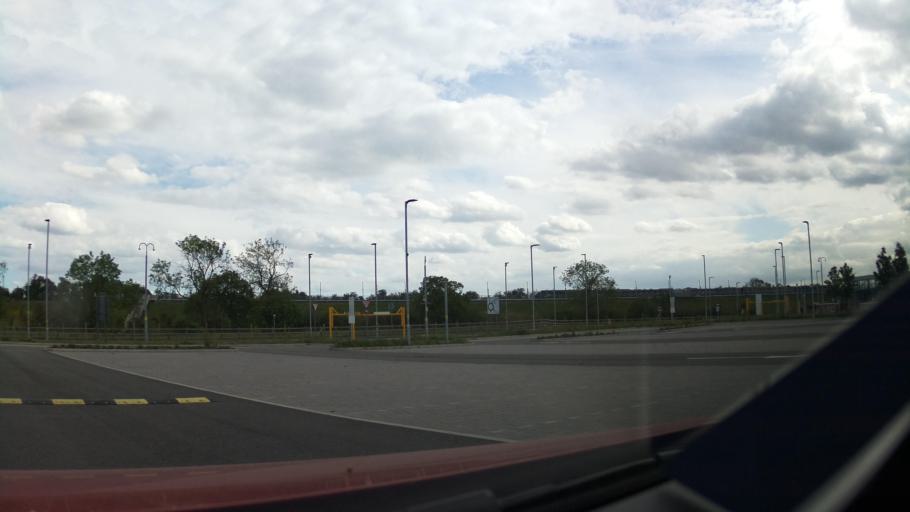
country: GB
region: England
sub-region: Worcestershire
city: Kempsey
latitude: 52.1578
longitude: -2.1577
